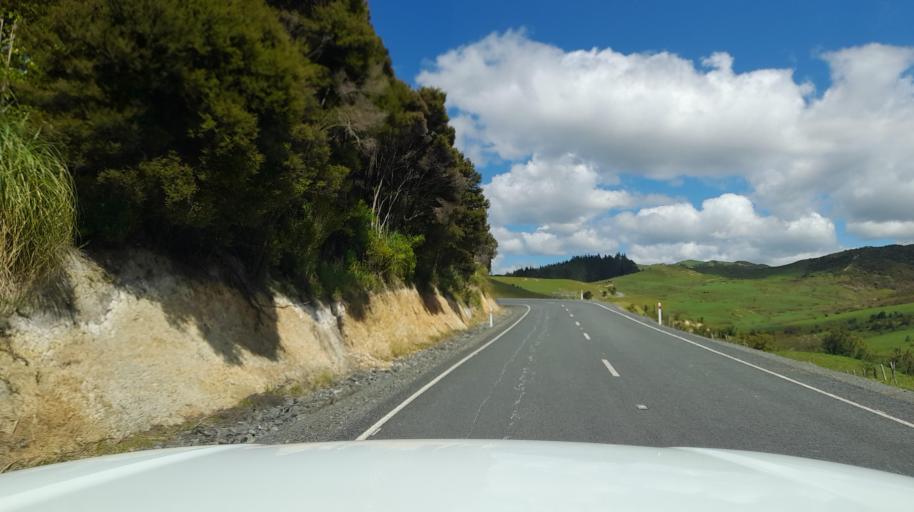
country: NZ
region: Northland
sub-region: Far North District
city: Taipa
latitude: -35.1001
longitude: 173.4671
